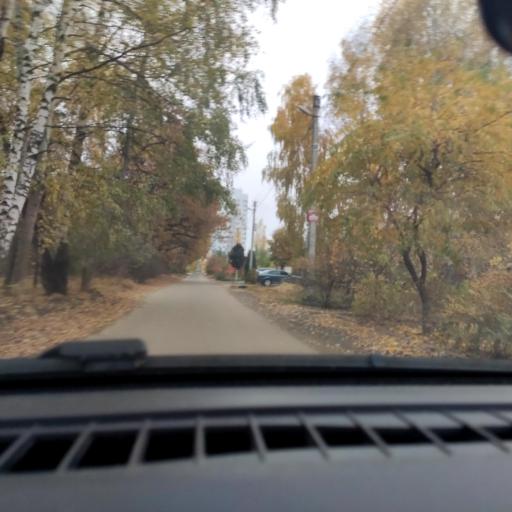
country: RU
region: Voronezj
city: Podgornoye
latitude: 51.7635
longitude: 39.1815
